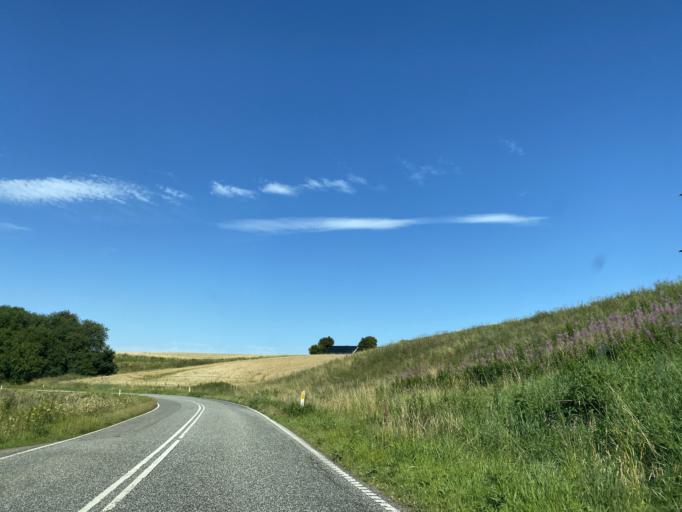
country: DK
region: Central Jutland
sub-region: Hedensted Kommune
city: Torring
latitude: 55.8210
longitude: 9.4556
